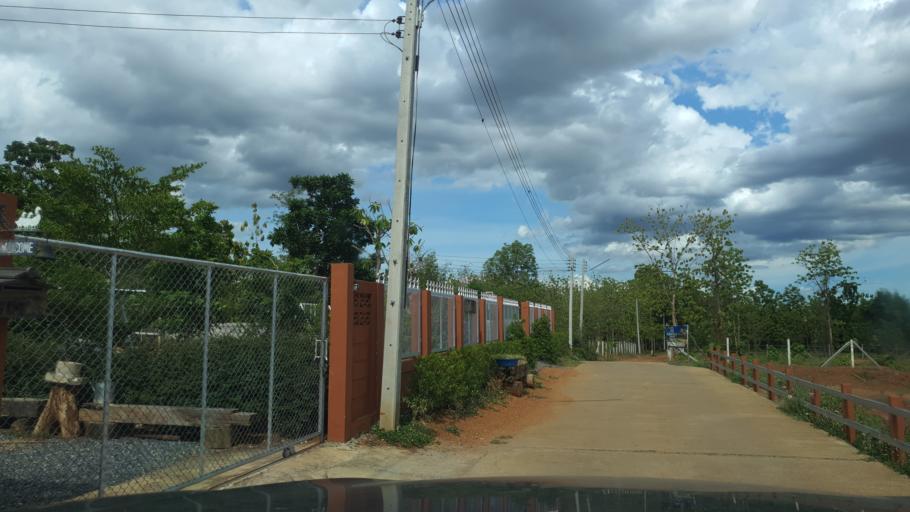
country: TH
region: Sukhothai
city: Thung Saliam
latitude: 17.3263
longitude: 99.5450
